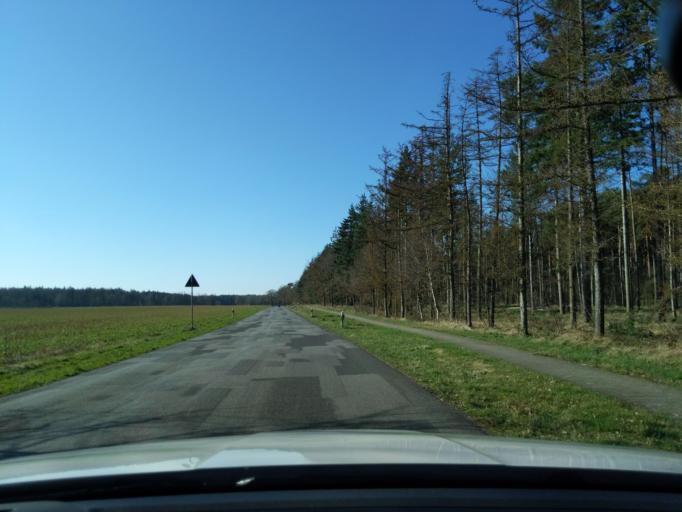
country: DE
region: Lower Saxony
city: Geeste
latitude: 52.6174
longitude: 7.2898
